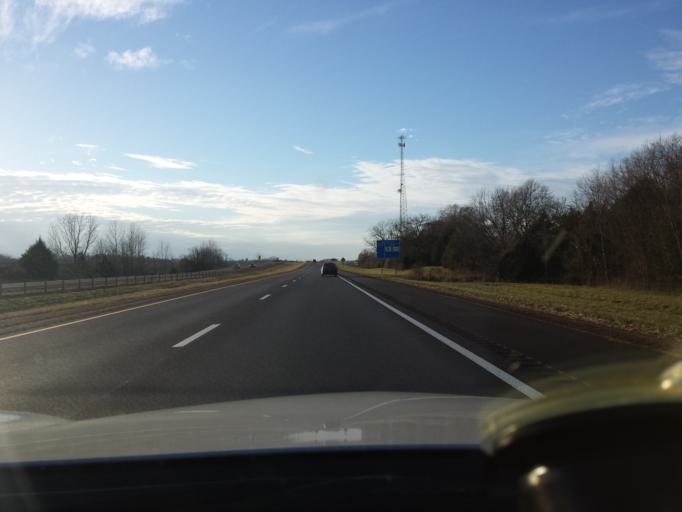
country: US
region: Mississippi
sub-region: Oktibbeha County
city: Starkville
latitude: 33.4692
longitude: -88.7490
